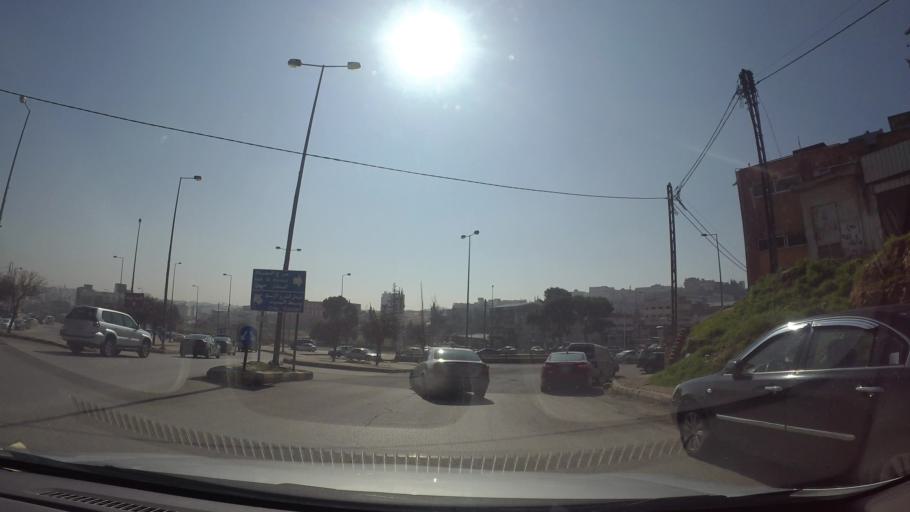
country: JO
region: Amman
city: Al Bunayyat ash Shamaliyah
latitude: 31.9171
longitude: 35.9028
